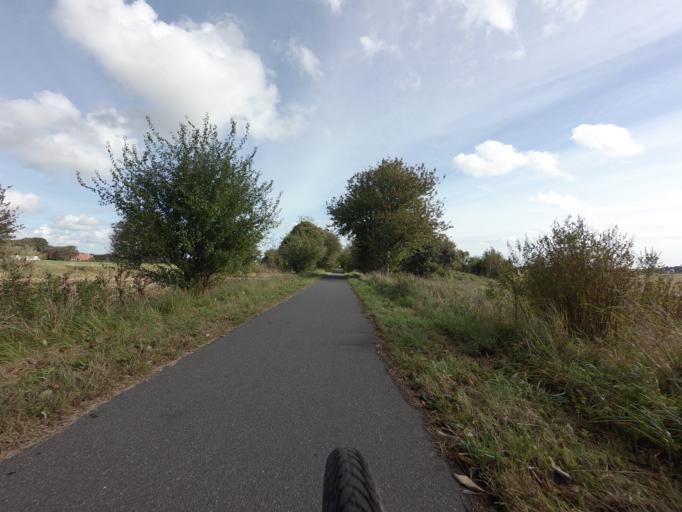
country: DK
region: Central Jutland
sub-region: Viborg Kommune
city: Bjerringbro
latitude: 56.4890
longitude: 9.6354
